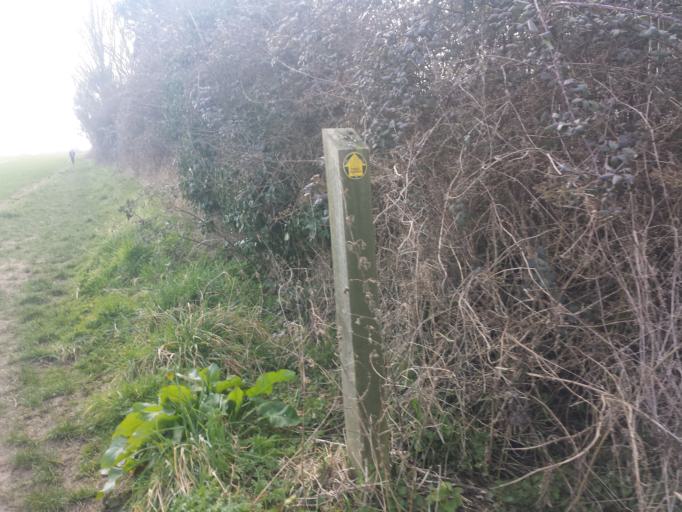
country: GB
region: England
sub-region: Essex
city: Mistley
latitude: 51.9124
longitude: 1.1490
